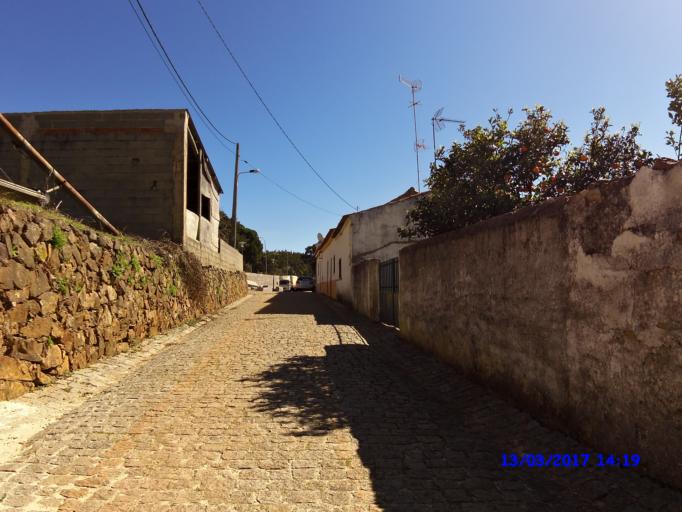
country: PT
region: Faro
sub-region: Monchique
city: Monchique
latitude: 37.3086
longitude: -8.6661
